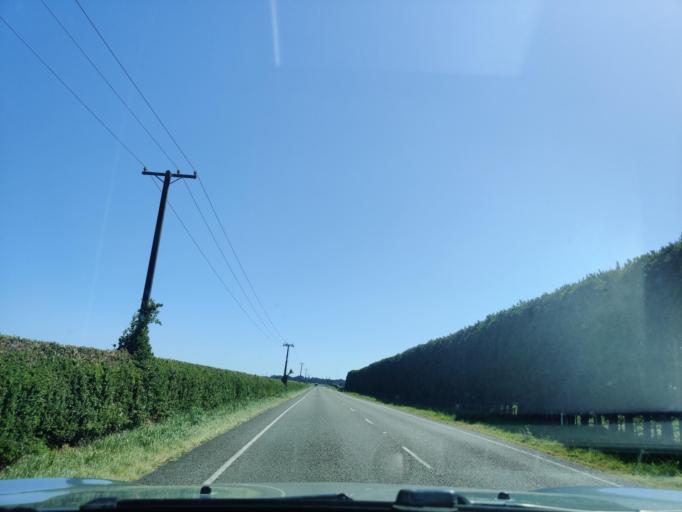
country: NZ
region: Taranaki
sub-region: South Taranaki District
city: Patea
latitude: -39.7880
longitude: 174.7002
